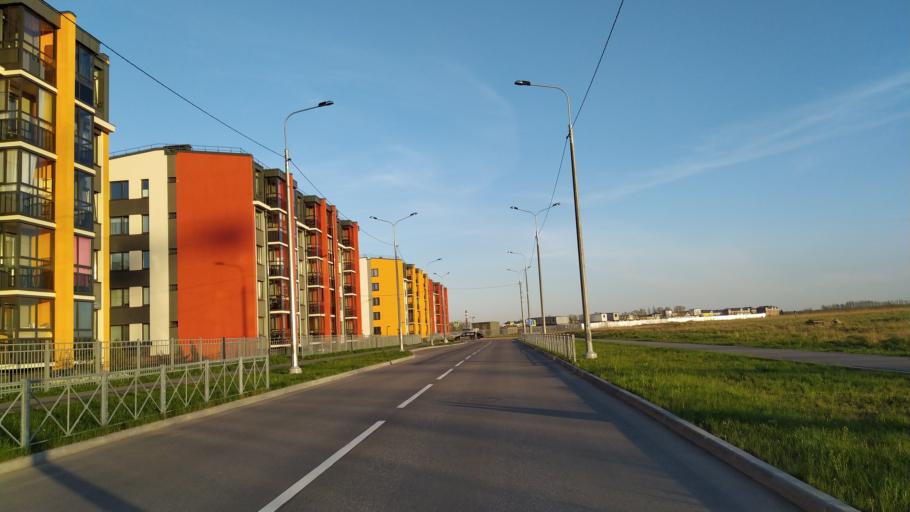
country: RU
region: St.-Petersburg
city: Pushkin
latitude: 59.6981
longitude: 30.4048
